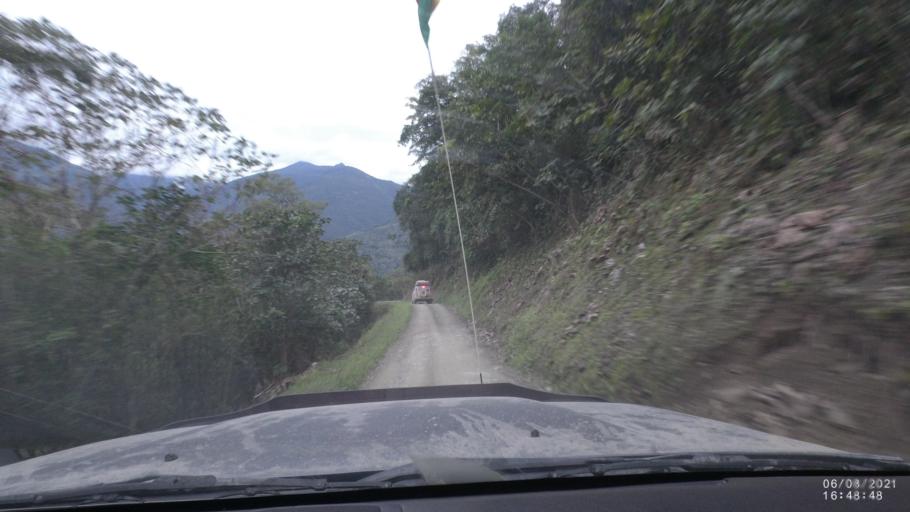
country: BO
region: La Paz
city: Quime
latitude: -16.5004
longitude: -66.7658
